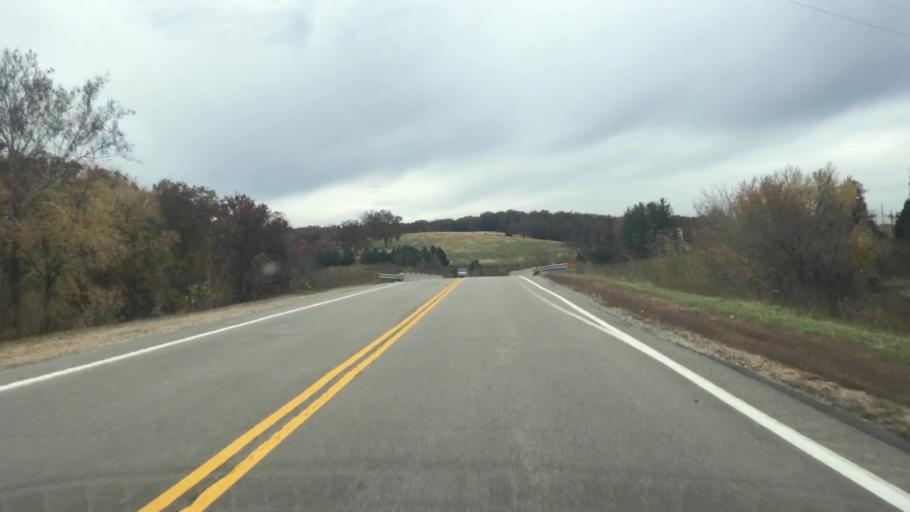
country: US
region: Missouri
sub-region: Gasconade County
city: Hermann
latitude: 38.7189
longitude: -91.6898
